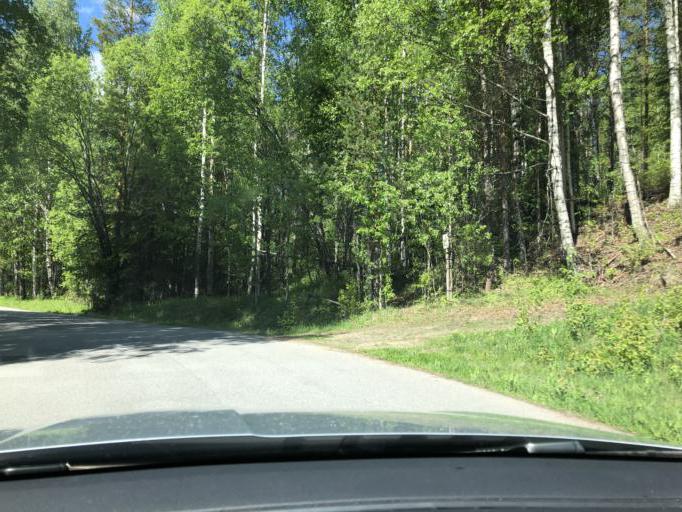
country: SE
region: Norrbotten
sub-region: Alvsbyns Kommun
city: AElvsbyn
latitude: 65.6682
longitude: 21.0223
